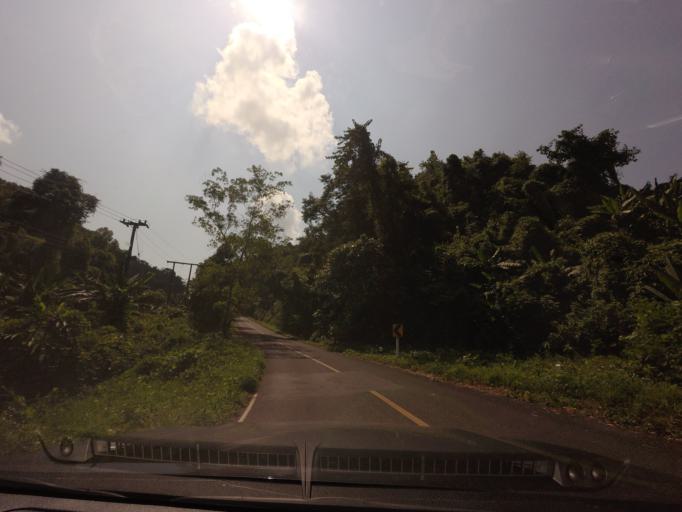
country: TH
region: Nan
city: Bo Kluea
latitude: 19.0509
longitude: 101.1668
